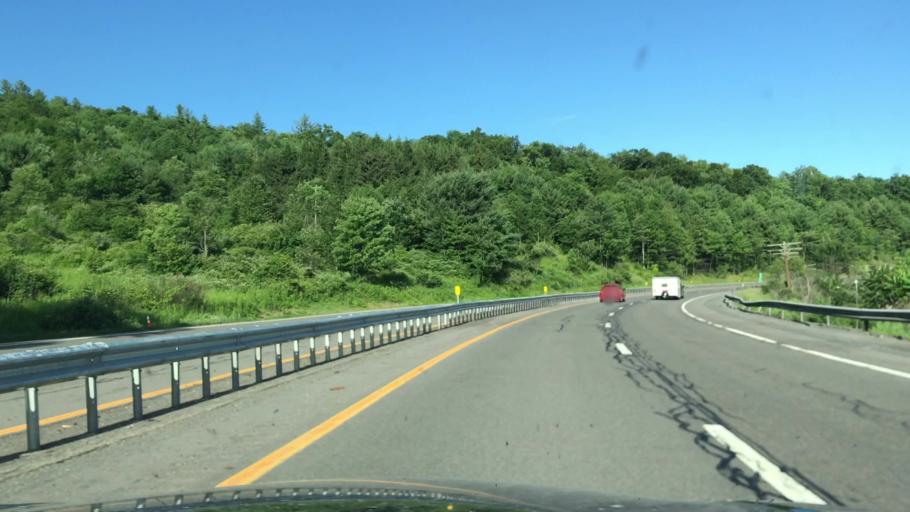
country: US
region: New York
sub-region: Broome County
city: Deposit
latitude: 42.0095
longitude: -75.3662
